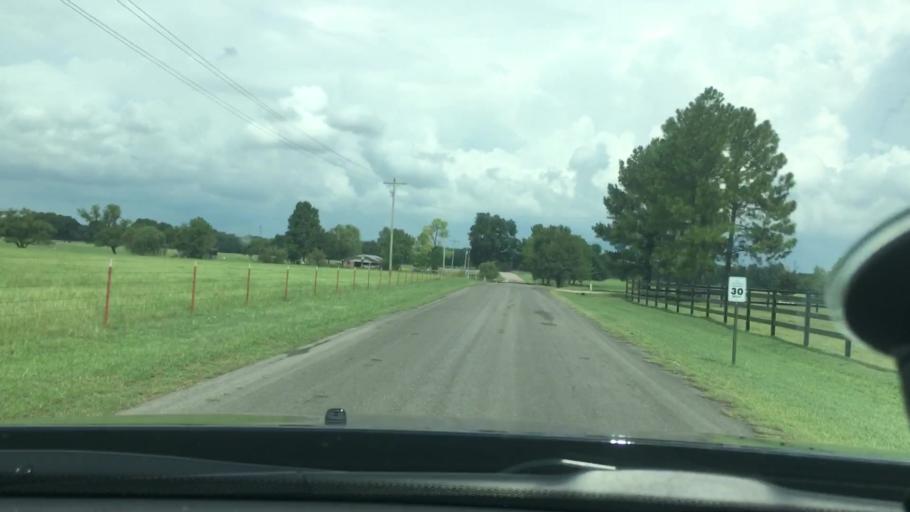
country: US
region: Oklahoma
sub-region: Carter County
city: Dickson
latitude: 34.2328
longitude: -96.9157
